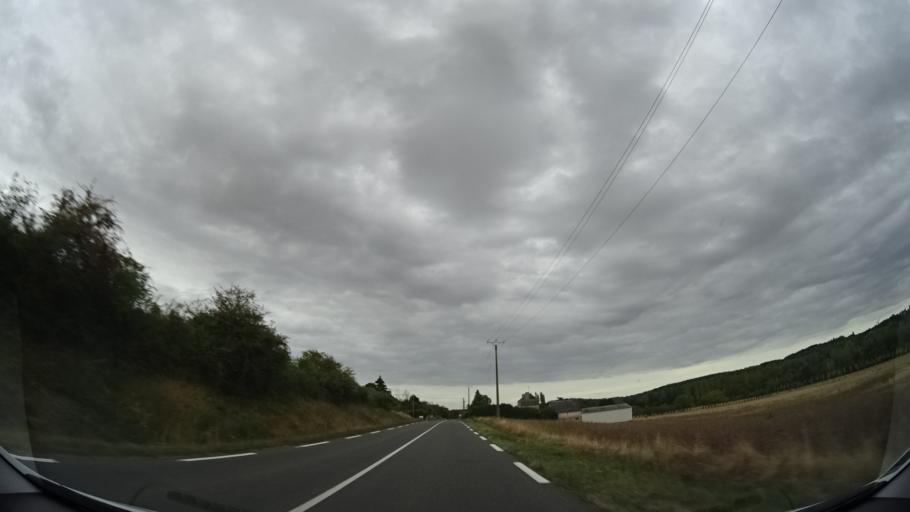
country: FR
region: Centre
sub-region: Departement du Loiret
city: Saint-Germain-des-Pres
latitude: 47.9348
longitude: 2.8982
